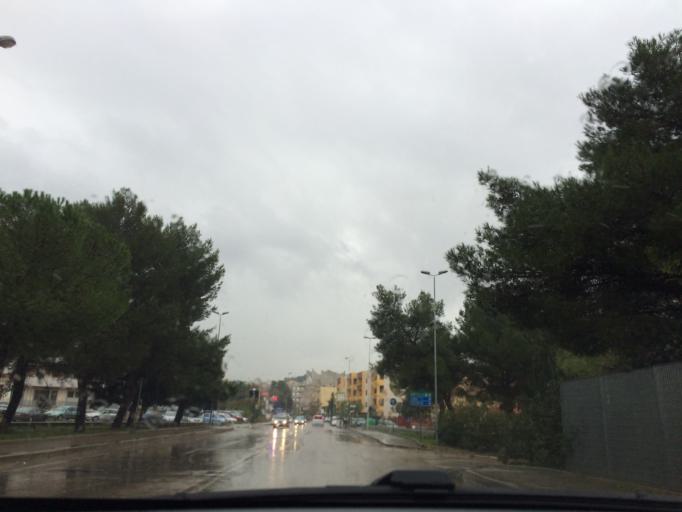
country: IT
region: Basilicate
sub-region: Provincia di Matera
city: Matera
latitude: 40.6795
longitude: 16.5862
